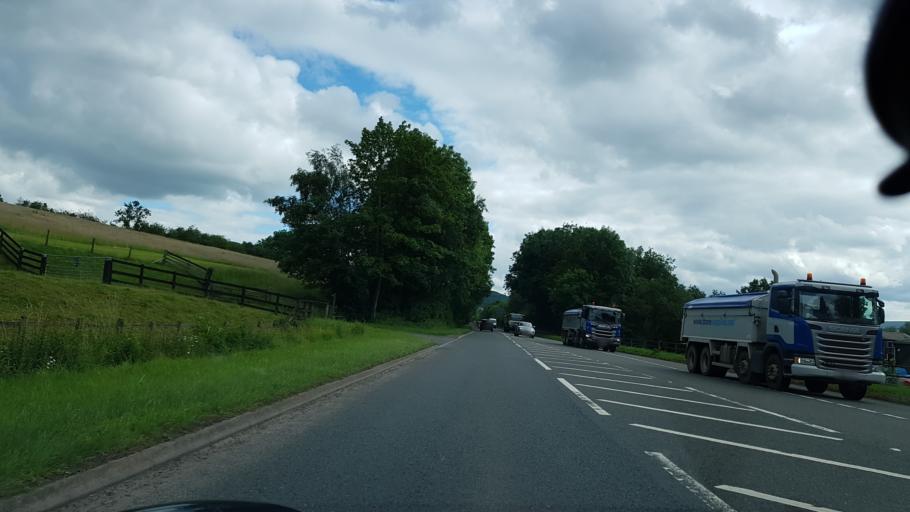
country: GB
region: Wales
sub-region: Monmouthshire
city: Abergavenny
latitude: 51.8500
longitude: -3.0014
